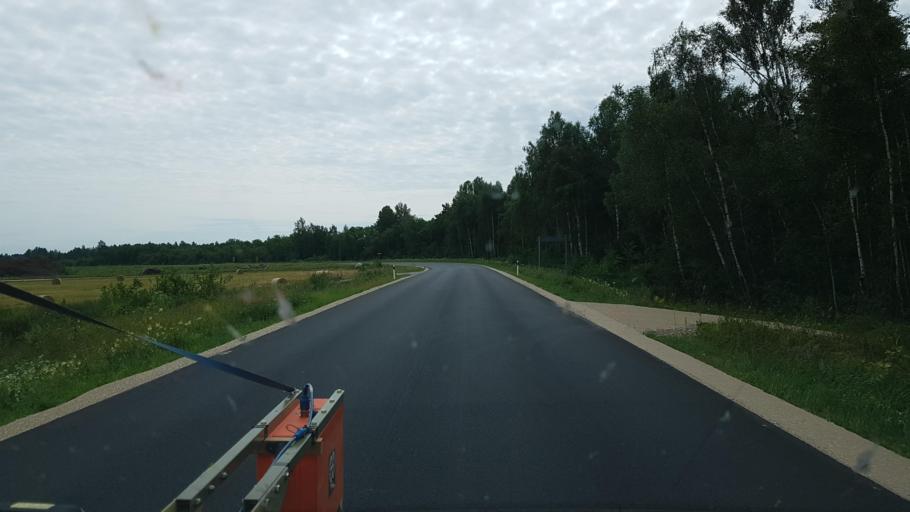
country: EE
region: Paernumaa
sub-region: Halinga vald
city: Parnu-Jaagupi
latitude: 58.6206
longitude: 24.2722
